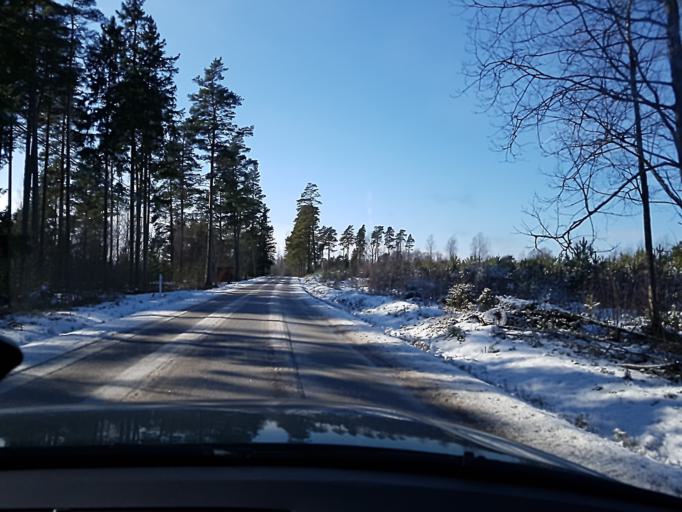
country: FI
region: Uusimaa
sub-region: Raaseporin
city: Inga
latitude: 60.0819
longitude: 24.0411
